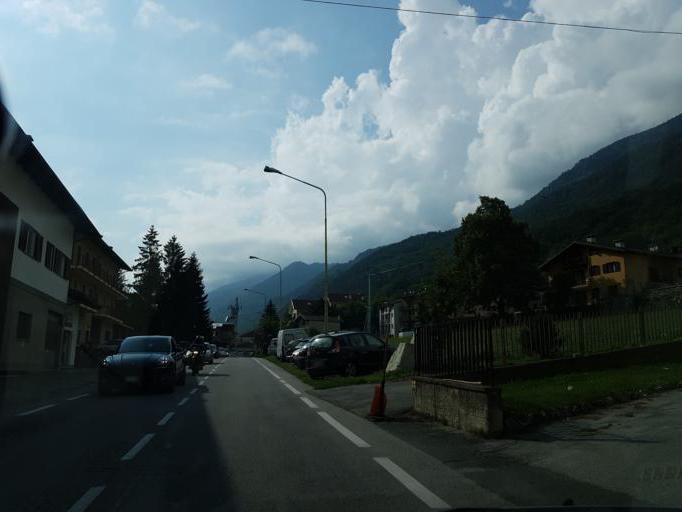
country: IT
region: Piedmont
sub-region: Provincia di Cuneo
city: Sampeyre
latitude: 44.5785
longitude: 7.1865
